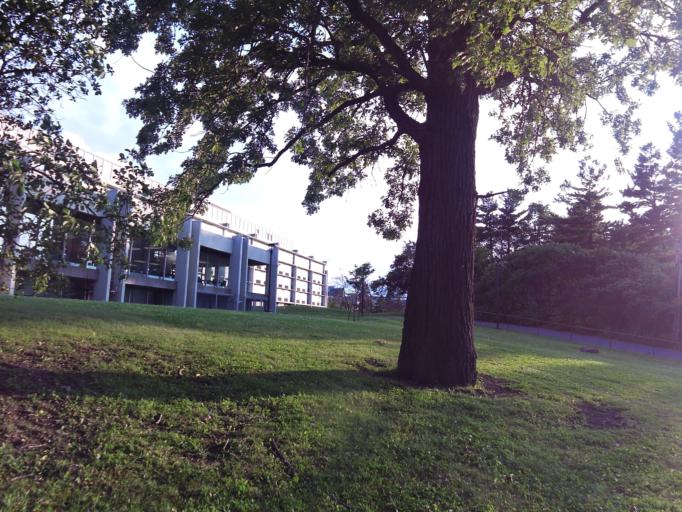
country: CA
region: Ontario
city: Ottawa
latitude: 45.3813
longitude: -75.6830
